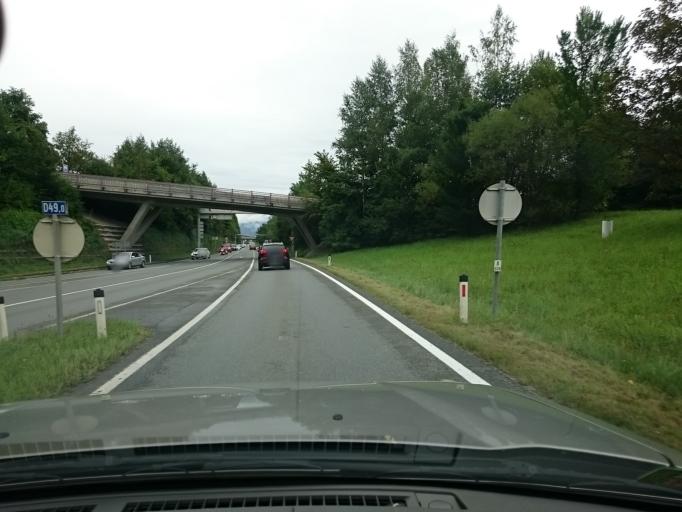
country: AT
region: Salzburg
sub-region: Politischer Bezirk Zell am See
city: Zell am See
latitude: 47.3454
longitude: 12.7992
